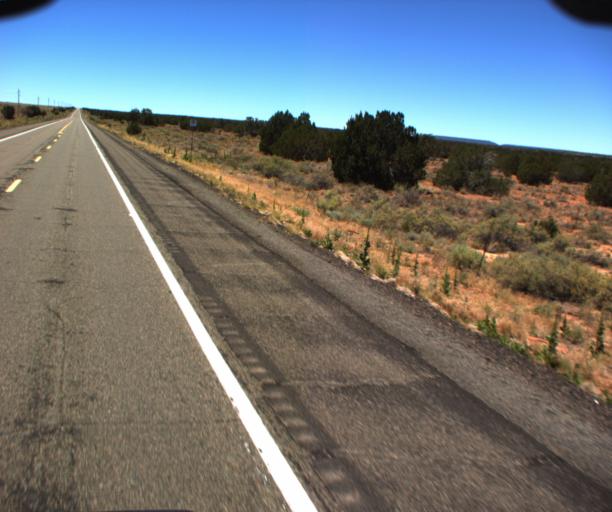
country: US
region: Arizona
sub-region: Coconino County
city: LeChee
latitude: 34.8188
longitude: -110.9636
